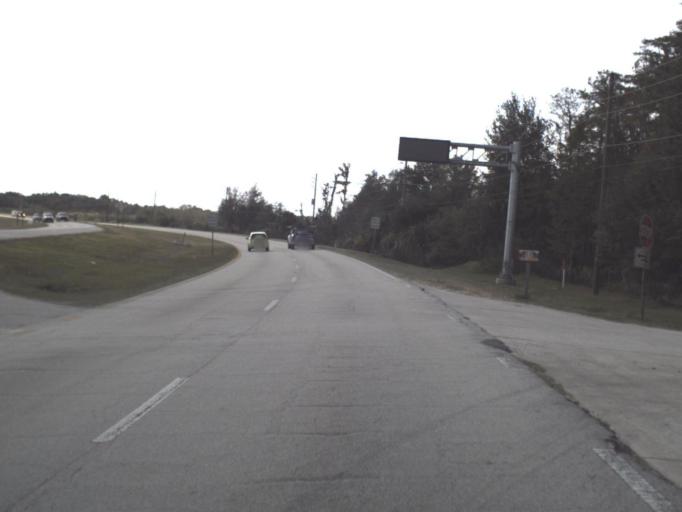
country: US
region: Florida
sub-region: Osceola County
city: Campbell
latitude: 28.2678
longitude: -81.4856
